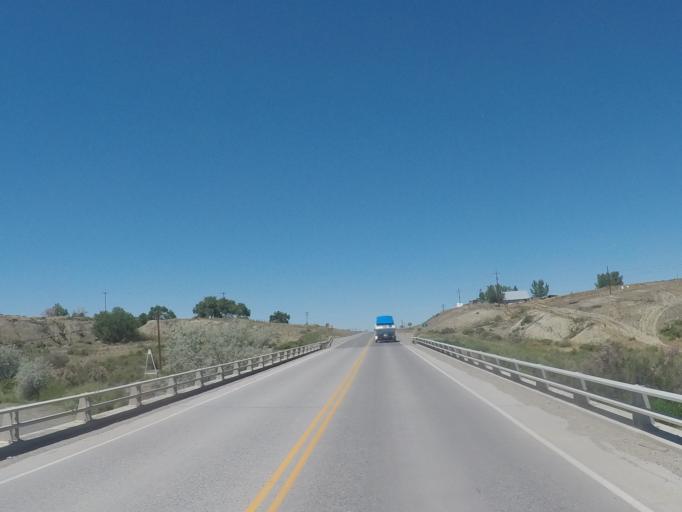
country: US
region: Wyoming
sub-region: Big Horn County
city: Lovell
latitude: 44.8389
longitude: -108.4332
